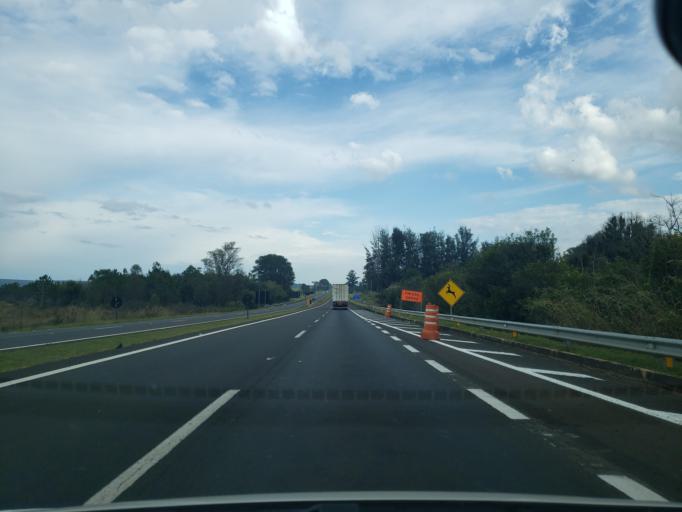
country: BR
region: Sao Paulo
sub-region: Itirapina
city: Itirapina
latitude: -22.2645
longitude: -47.9097
